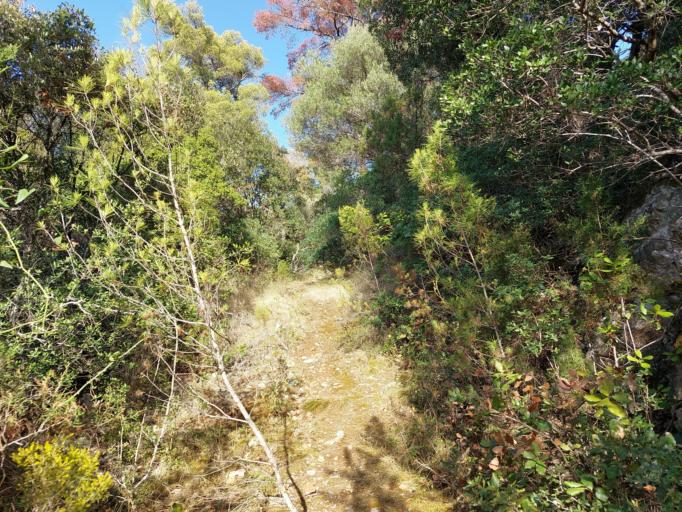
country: HR
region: Dubrovacko-Neretvanska
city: Smokvica
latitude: 42.7556
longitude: 16.8127
